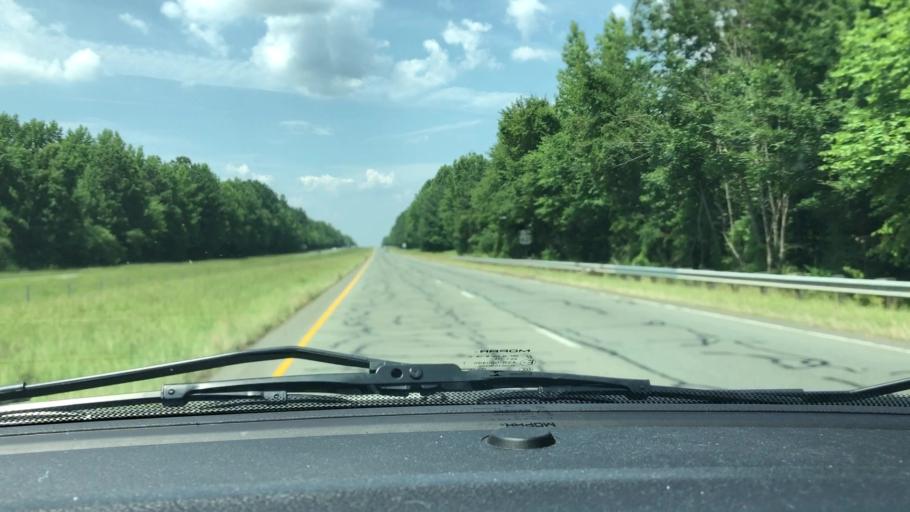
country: US
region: North Carolina
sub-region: Chatham County
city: Siler City
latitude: 35.7015
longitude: -79.4285
